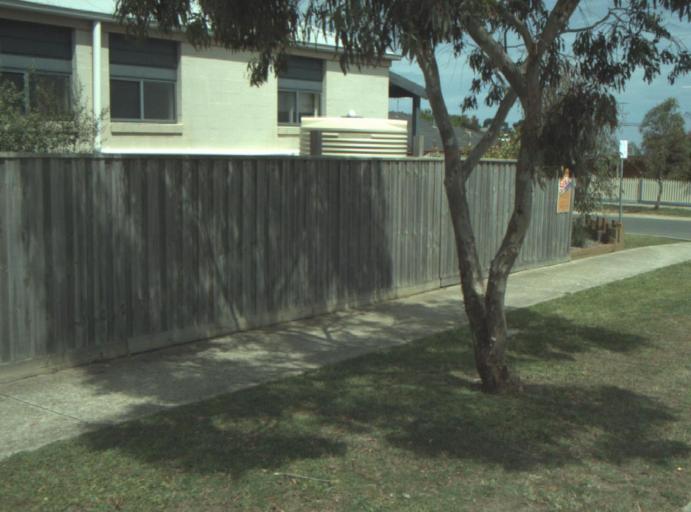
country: AU
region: Victoria
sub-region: Greater Geelong
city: Clifton Springs
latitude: -38.2524
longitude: 144.5569
